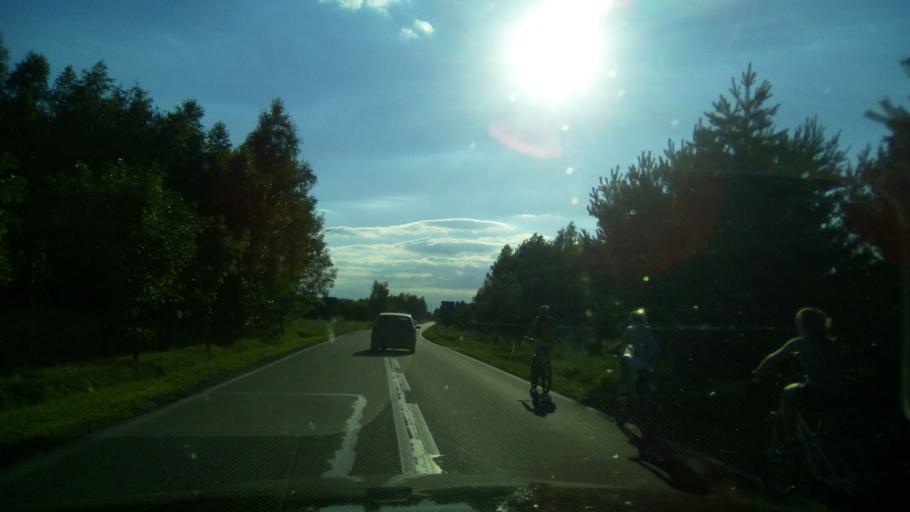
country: PL
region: Masovian Voivodeship
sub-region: Powiat radomski
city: Jastrzebia
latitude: 51.6171
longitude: 21.2265
